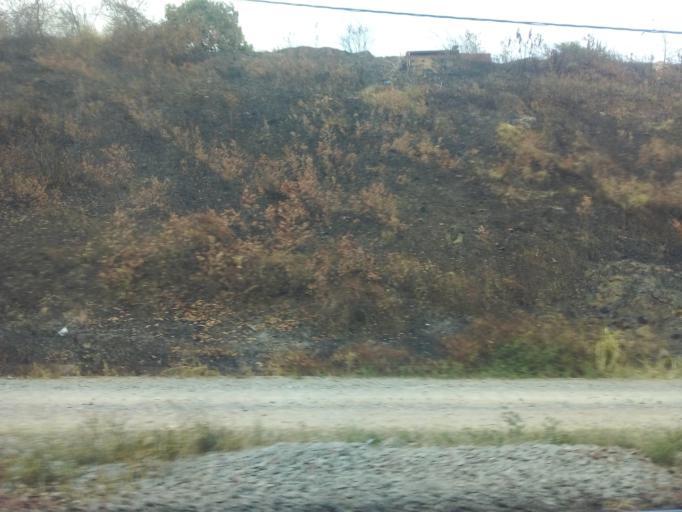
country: BR
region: Maranhao
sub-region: Sao Luis
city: Sao Luis
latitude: -2.6245
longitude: -44.3096
